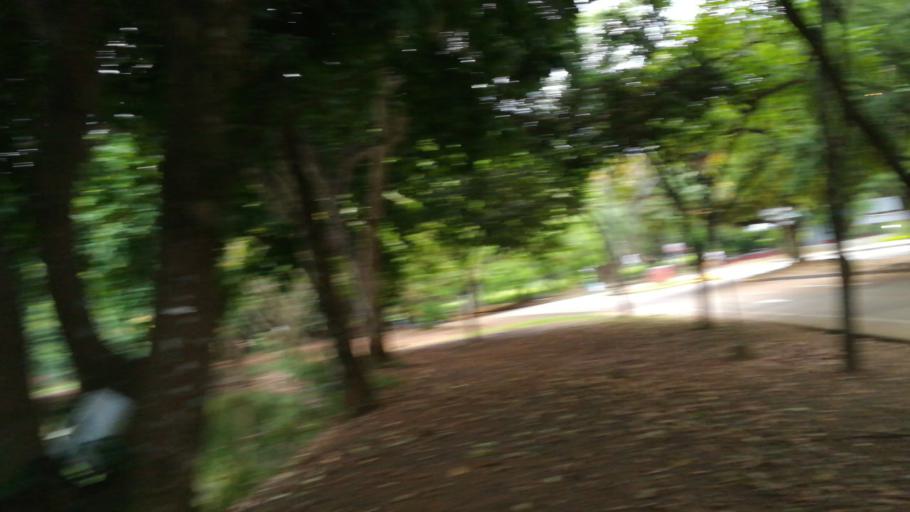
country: CO
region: Valle del Cauca
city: Cali
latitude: 3.3738
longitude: -76.5340
